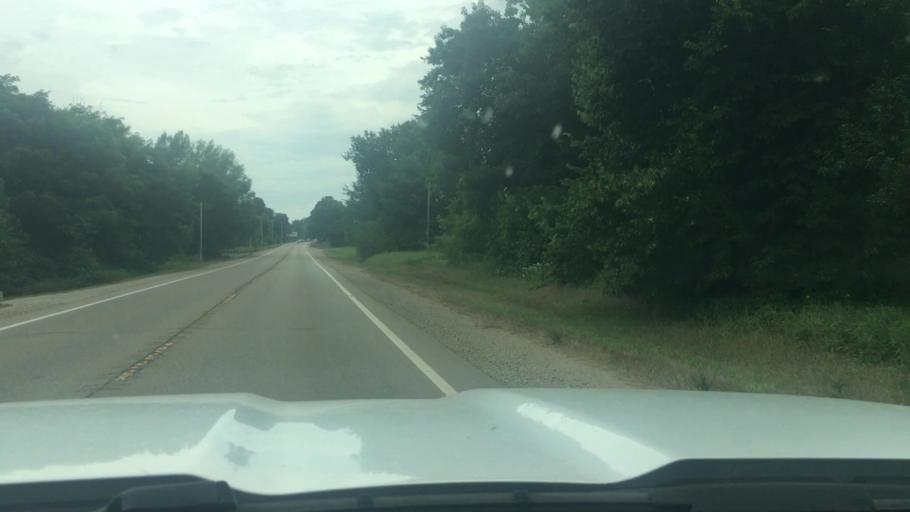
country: US
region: Michigan
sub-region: Kent County
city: Lowell
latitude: 42.9369
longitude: -85.2895
